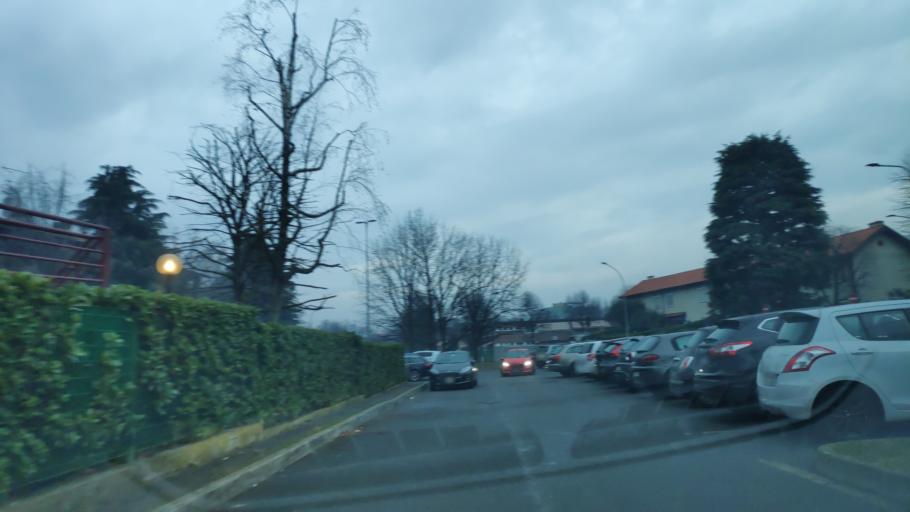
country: IT
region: Lombardy
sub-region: Citta metropolitana di Milano
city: Assago
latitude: 45.4174
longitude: 9.1264
